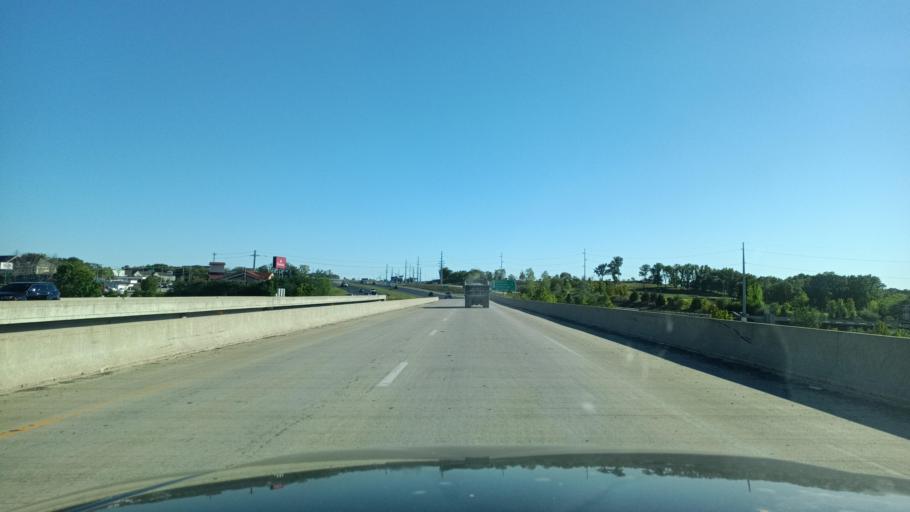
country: US
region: Missouri
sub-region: Boone County
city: Columbia
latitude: 38.9634
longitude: -92.2949
